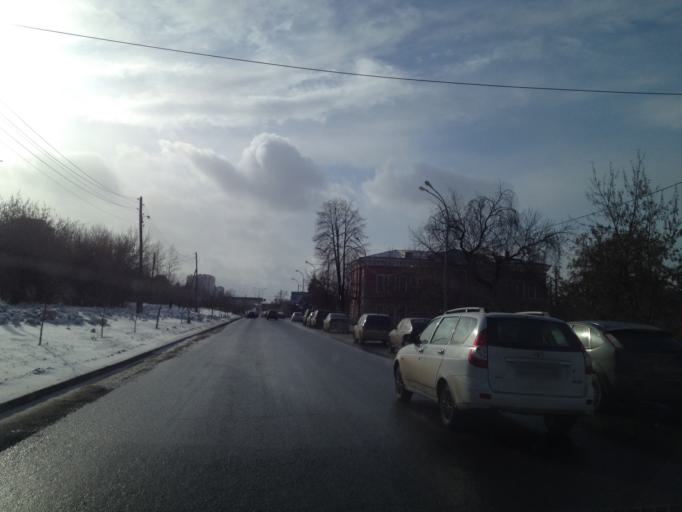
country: RU
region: Sverdlovsk
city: Yekaterinburg
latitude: 56.8397
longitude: 60.5668
